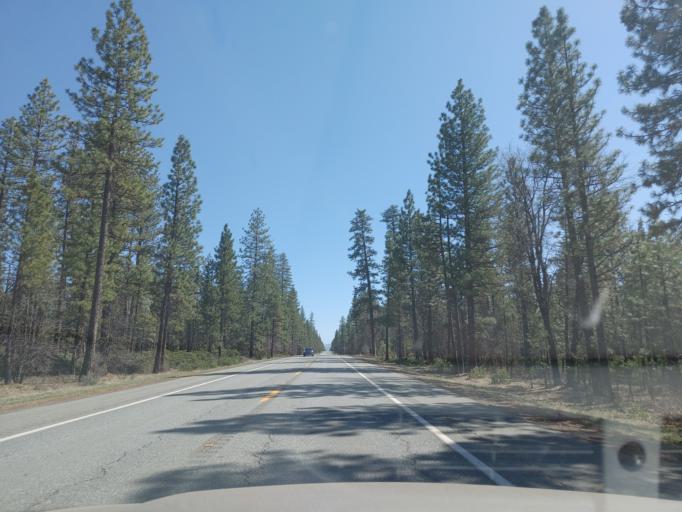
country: US
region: California
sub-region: Shasta County
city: Burney
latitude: 40.9794
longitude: -121.6227
